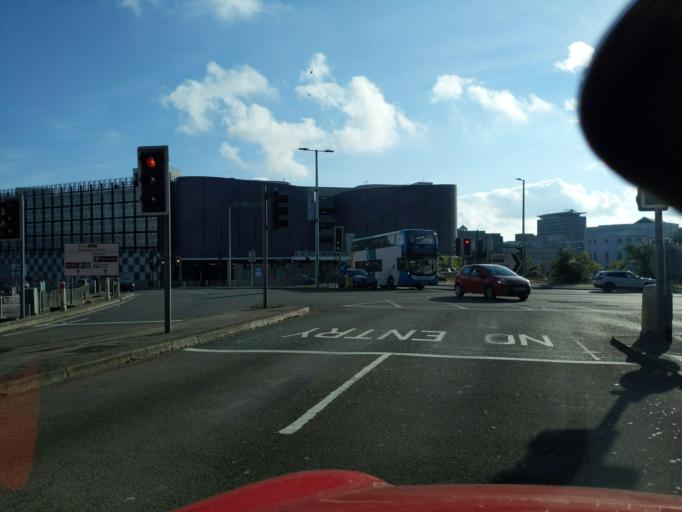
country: GB
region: England
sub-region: Plymouth
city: Plymouth
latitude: 50.3739
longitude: -4.1384
